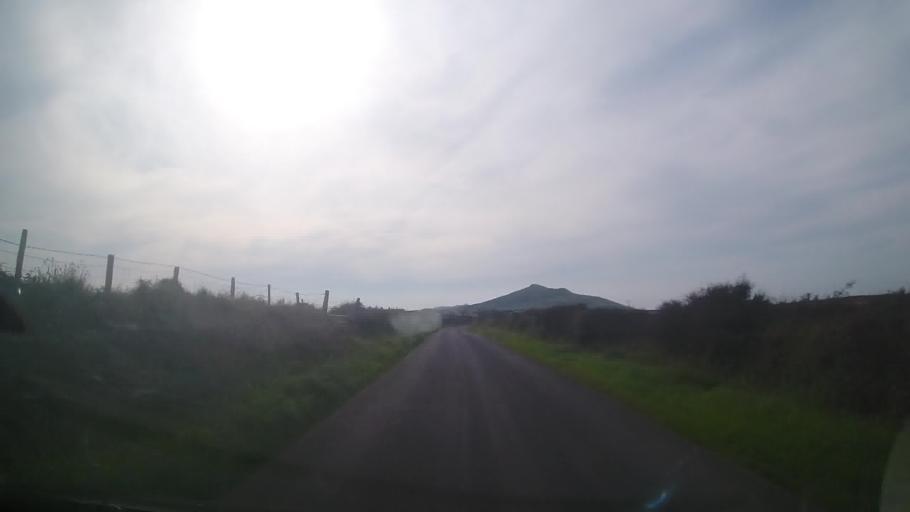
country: GB
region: Wales
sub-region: Pembrokeshire
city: Saint David's
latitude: 51.9200
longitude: -5.2271
